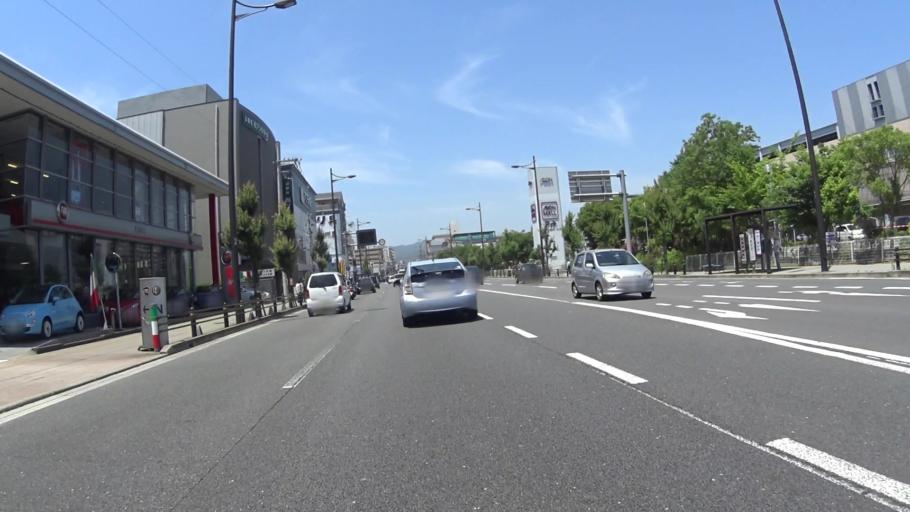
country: JP
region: Kyoto
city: Kyoto
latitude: 34.9961
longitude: 135.7274
